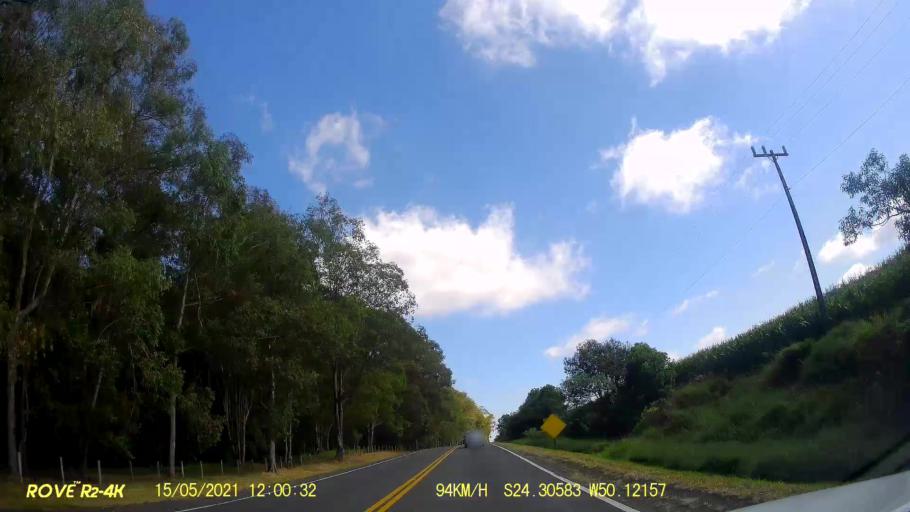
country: BR
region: Parana
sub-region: Pirai Do Sul
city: Pirai do Sul
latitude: -24.3059
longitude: -50.1209
